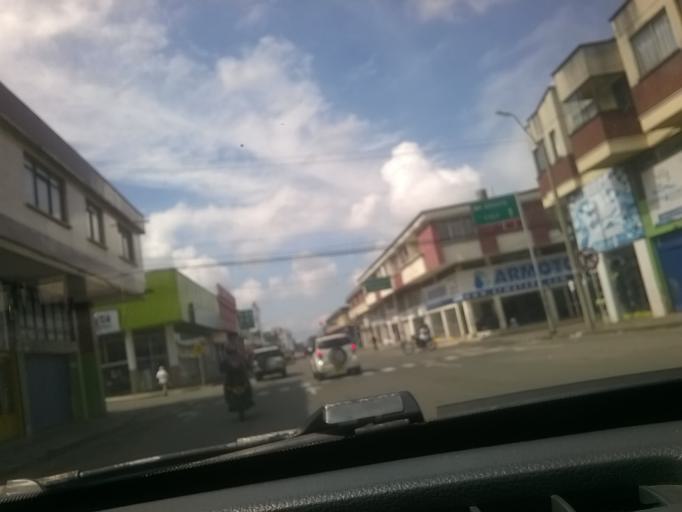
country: CO
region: Quindio
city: Armenia
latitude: 4.5392
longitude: -75.6711
